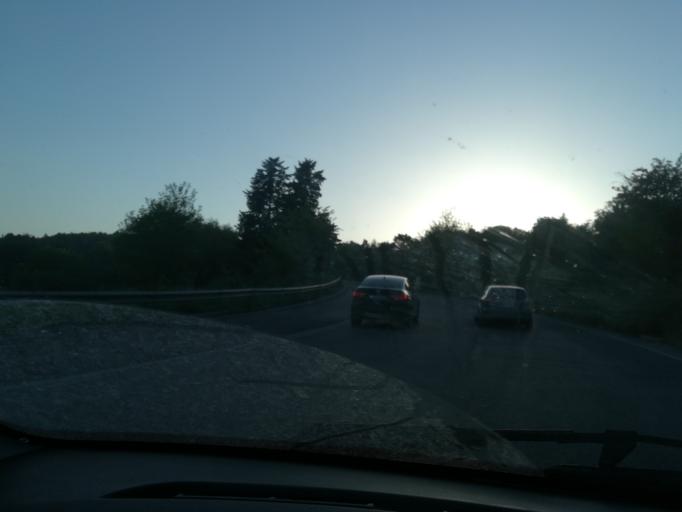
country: IT
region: The Marches
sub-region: Provincia di Macerata
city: Piediripa
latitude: 43.2855
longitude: 13.4786
